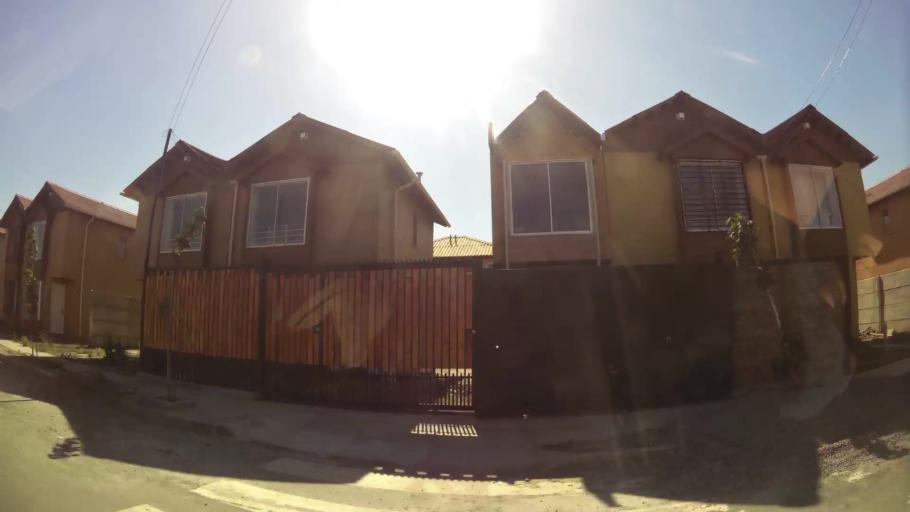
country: CL
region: Santiago Metropolitan
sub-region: Provincia de Maipo
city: San Bernardo
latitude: -33.6117
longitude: -70.6793
